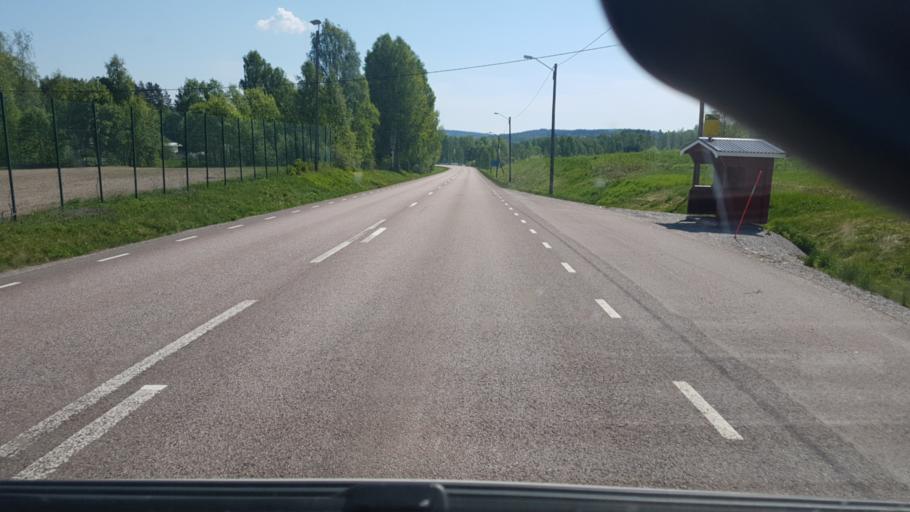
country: SE
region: Vaermland
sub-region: Eda Kommun
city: Amotfors
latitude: 59.6790
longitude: 12.4096
